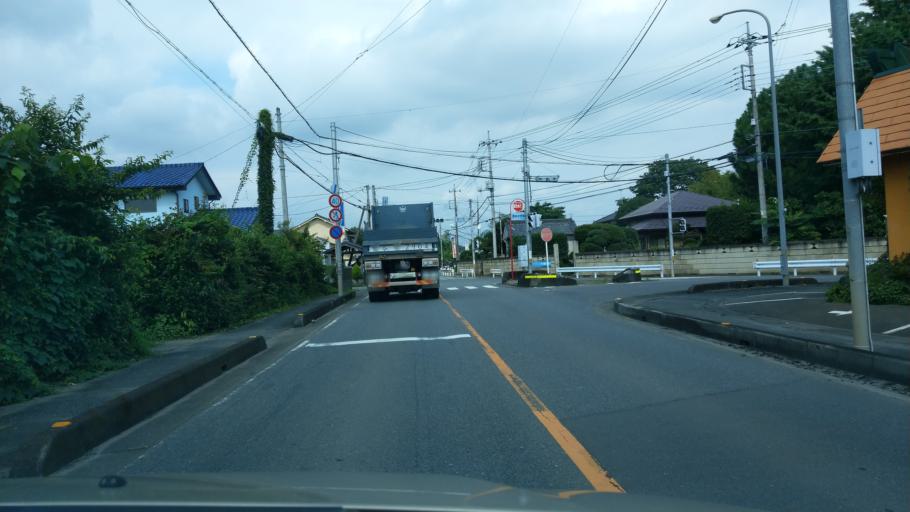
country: JP
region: Saitama
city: Sakado
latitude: 36.0323
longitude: 139.3489
